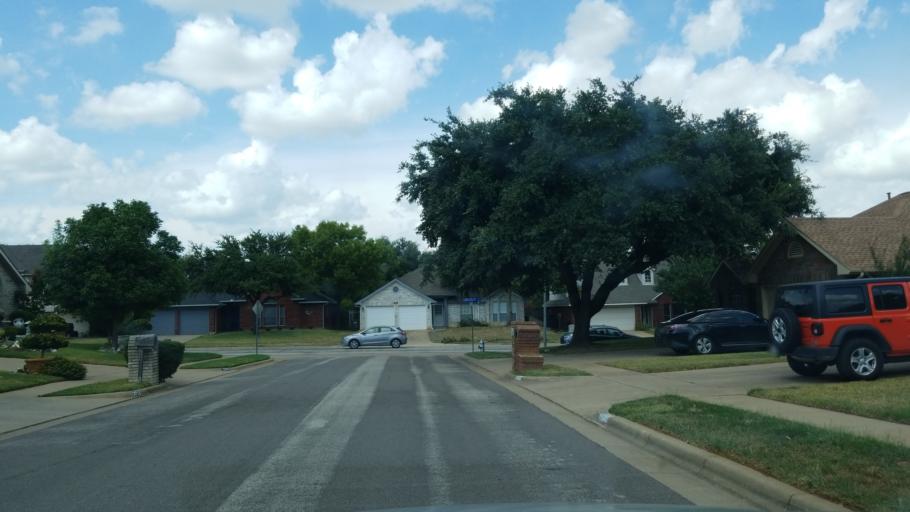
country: US
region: Texas
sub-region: Tarrant County
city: Euless
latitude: 32.8767
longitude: -97.0894
